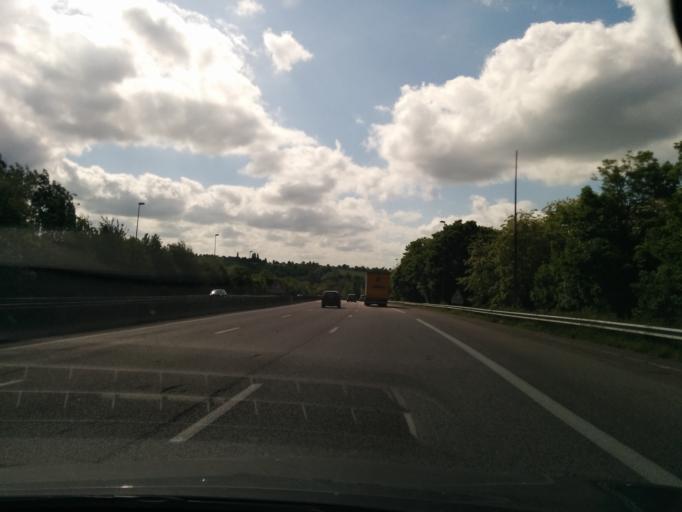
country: FR
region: Ile-de-France
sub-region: Departement des Yvelines
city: Guerville
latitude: 48.9686
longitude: 1.7420
